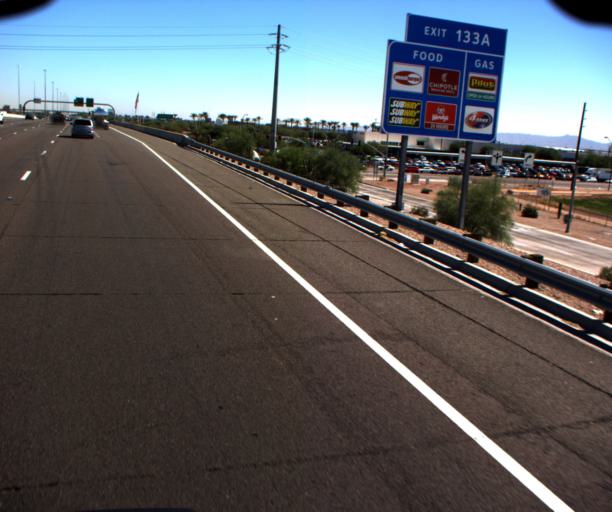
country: US
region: Arizona
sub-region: Maricopa County
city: Tolleson
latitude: 33.4611
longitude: -112.2912
